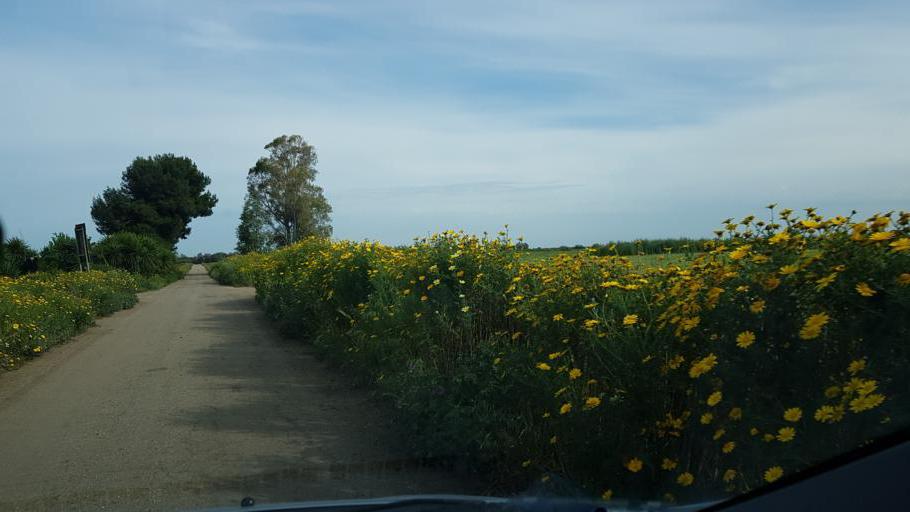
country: IT
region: Apulia
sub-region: Provincia di Brindisi
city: Tuturano
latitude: 40.5338
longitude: 17.9555
